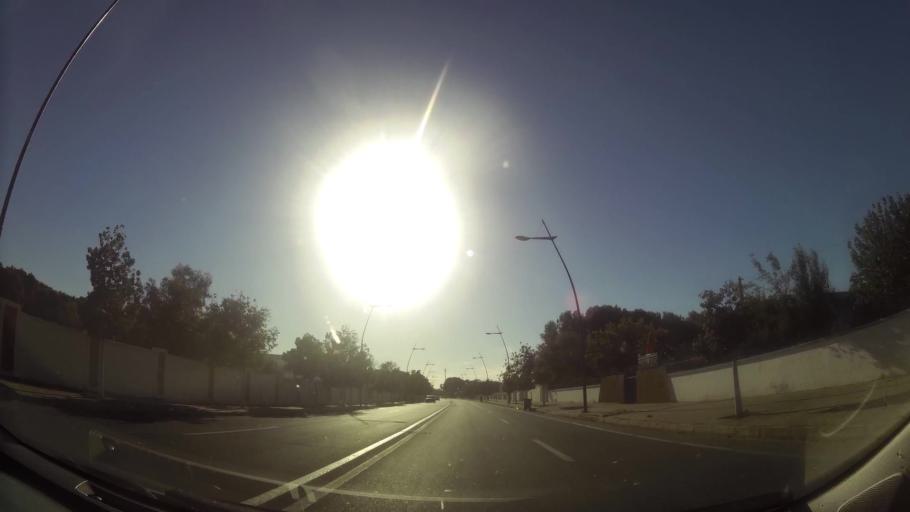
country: MA
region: Oriental
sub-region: Berkane-Taourirt
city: Madagh
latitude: 35.0882
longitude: -2.2384
